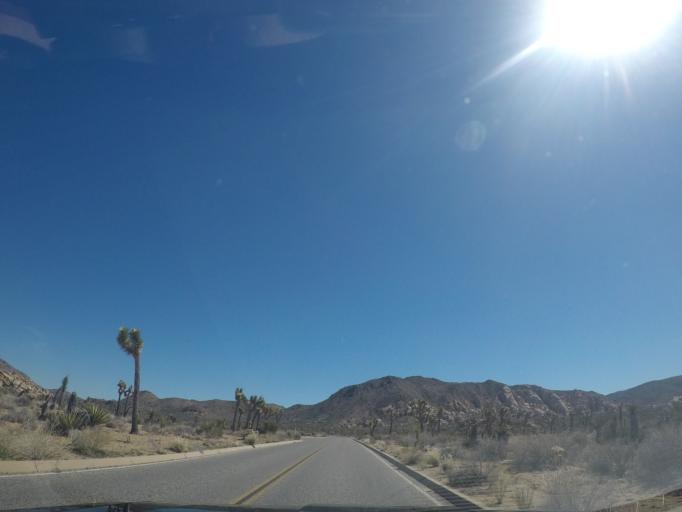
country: US
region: California
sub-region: San Bernardino County
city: Twentynine Palms
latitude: 34.0214
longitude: -116.1535
